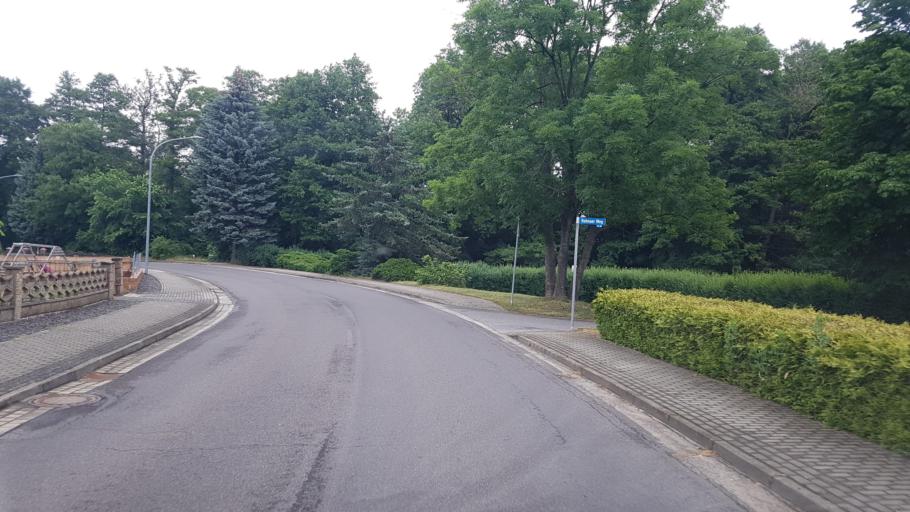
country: DE
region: Brandenburg
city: Hermsdorf
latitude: 51.3973
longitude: 13.8512
